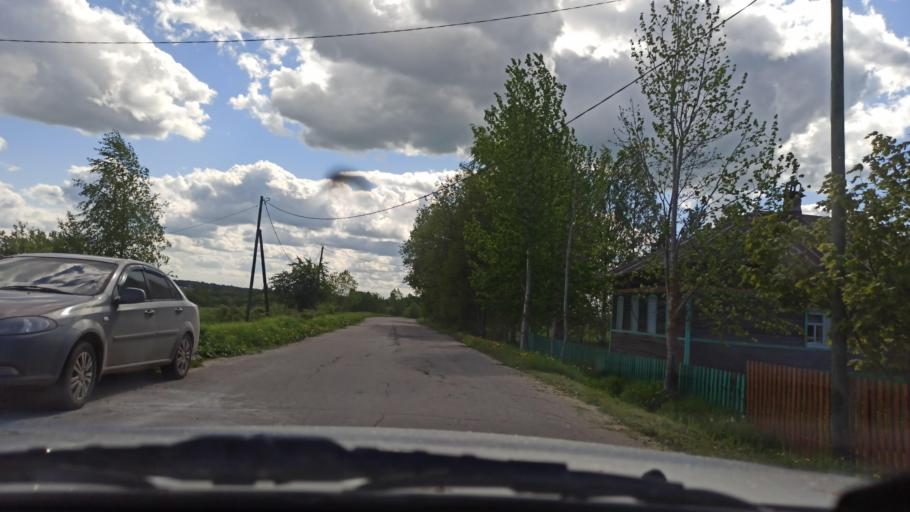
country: RU
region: Vologda
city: Molochnoye
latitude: 59.3779
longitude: 39.7165
